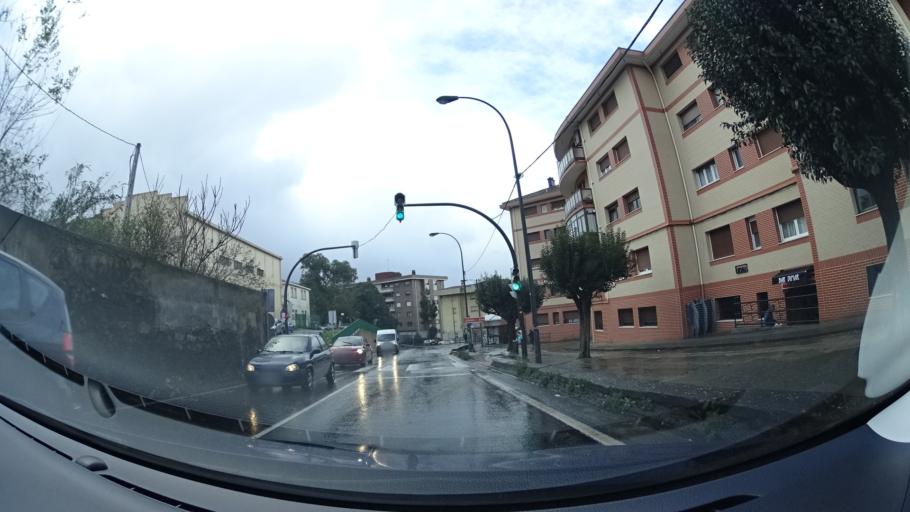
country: ES
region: Basque Country
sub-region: Bizkaia
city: Santutxu
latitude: 43.2615
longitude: -2.9103
